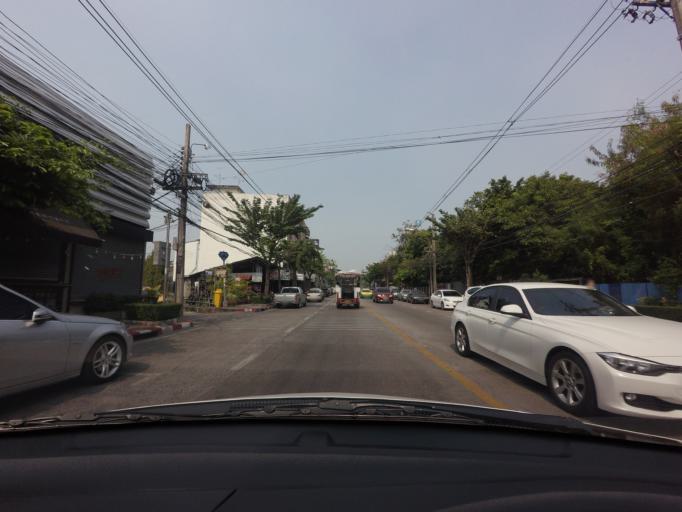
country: TH
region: Bangkok
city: Taling Chan
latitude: 13.7735
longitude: 100.4670
